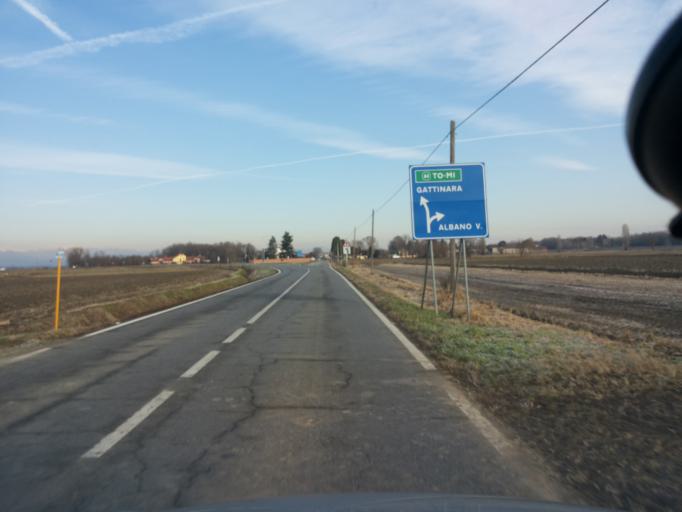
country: IT
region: Piedmont
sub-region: Provincia di Vercelli
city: Albano Vercellese
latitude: 45.4183
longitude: 8.3795
